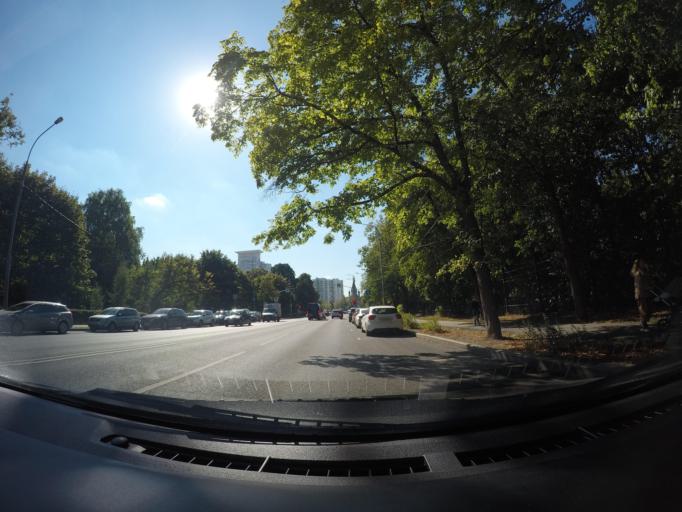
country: RU
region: Moscow
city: Sokol'niki
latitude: 55.7942
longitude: 37.6804
